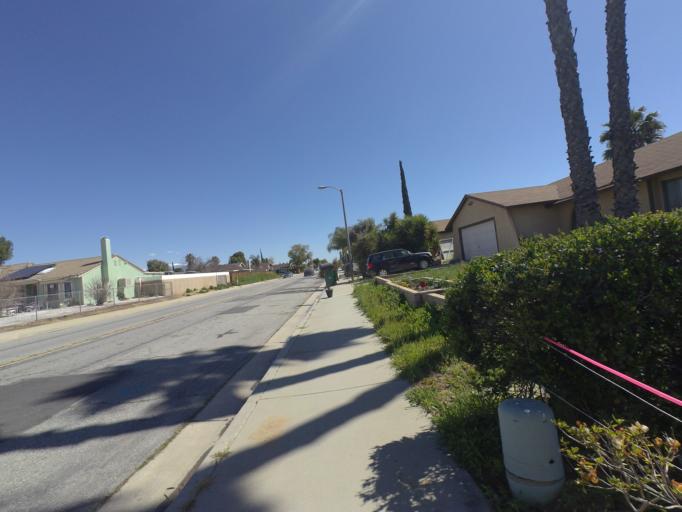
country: US
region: California
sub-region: Riverside County
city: Moreno Valley
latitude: 33.9136
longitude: -117.2400
